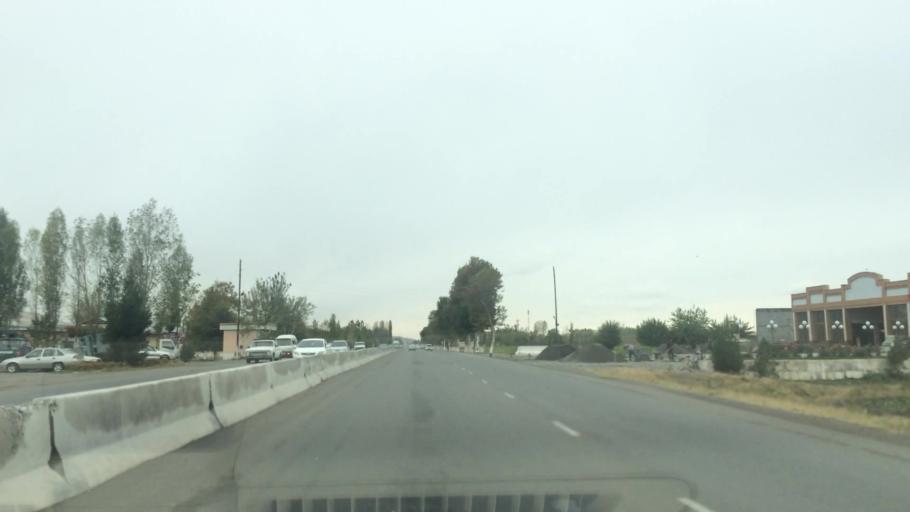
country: UZ
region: Samarqand
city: Jomboy
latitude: 39.7188
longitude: 67.1150
